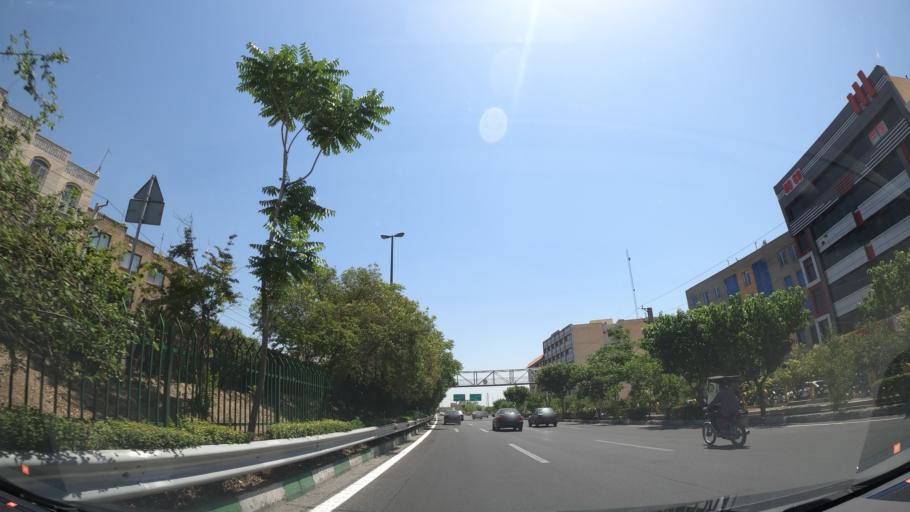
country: IR
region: Tehran
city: Tajrish
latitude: 35.7630
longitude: 51.2927
